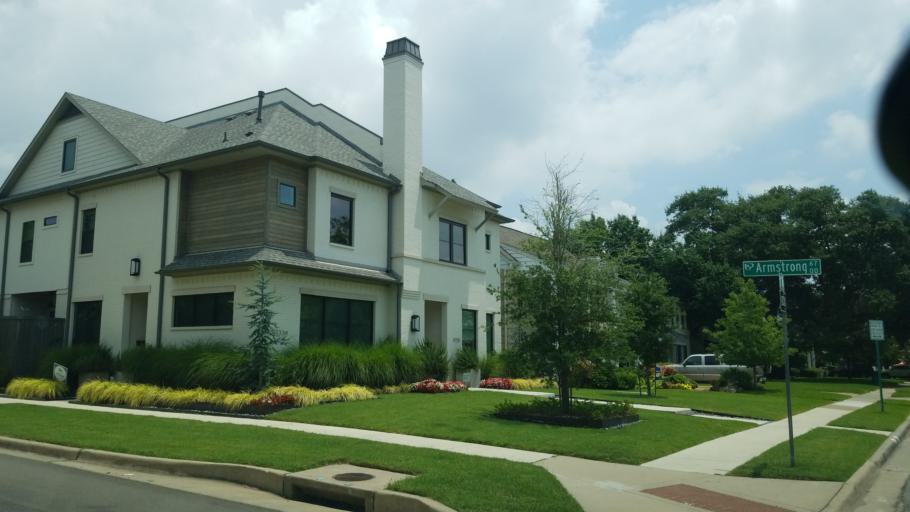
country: US
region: Texas
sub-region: Dallas County
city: University Park
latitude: 32.8474
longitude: -96.8104
